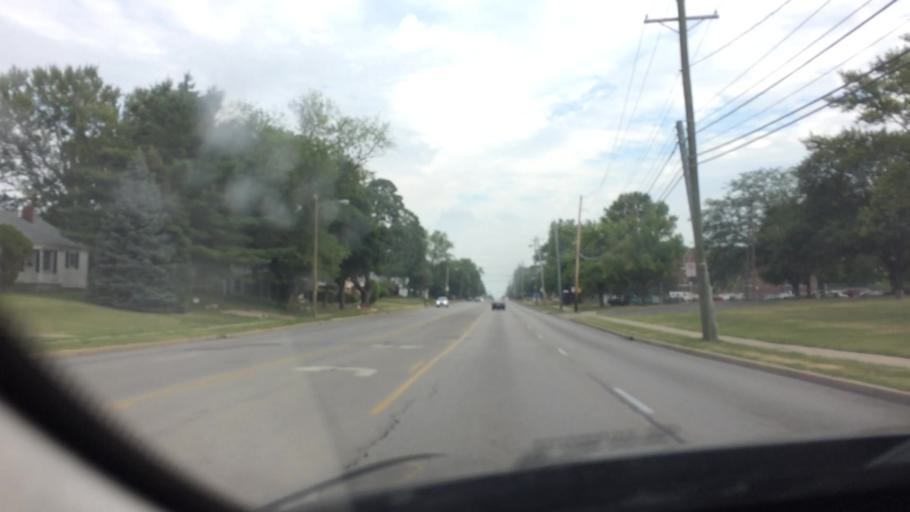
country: US
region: Ohio
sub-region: Lucas County
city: Ottawa Hills
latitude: 41.6509
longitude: -83.6260
